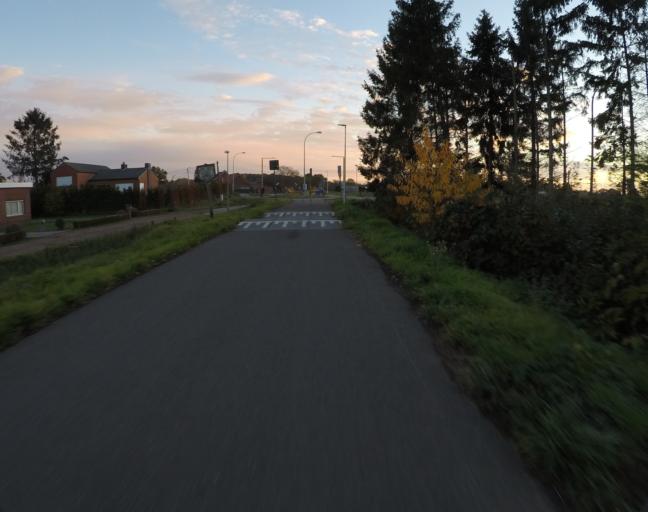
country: BE
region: Flanders
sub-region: Provincie Antwerpen
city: Herentals
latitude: 51.1521
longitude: 4.8206
